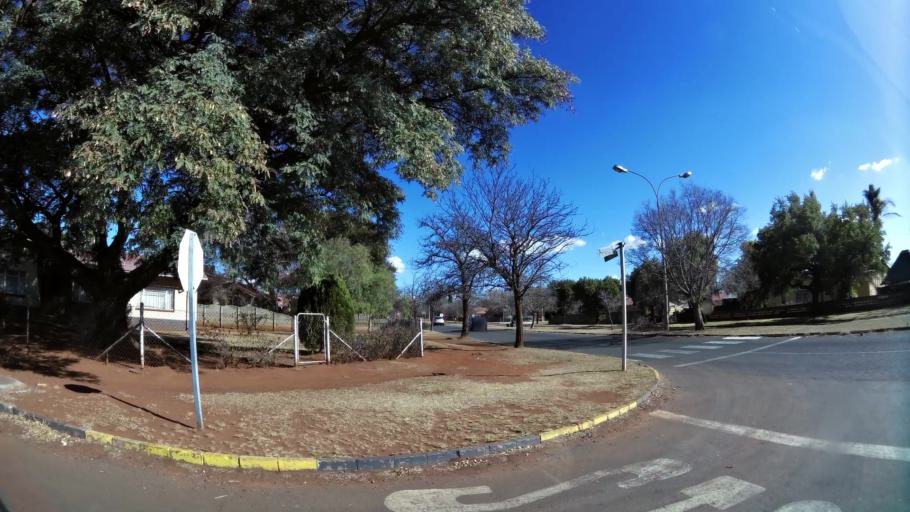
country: ZA
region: Gauteng
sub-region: West Rand District Municipality
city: Carletonville
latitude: -26.3645
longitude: 27.3795
